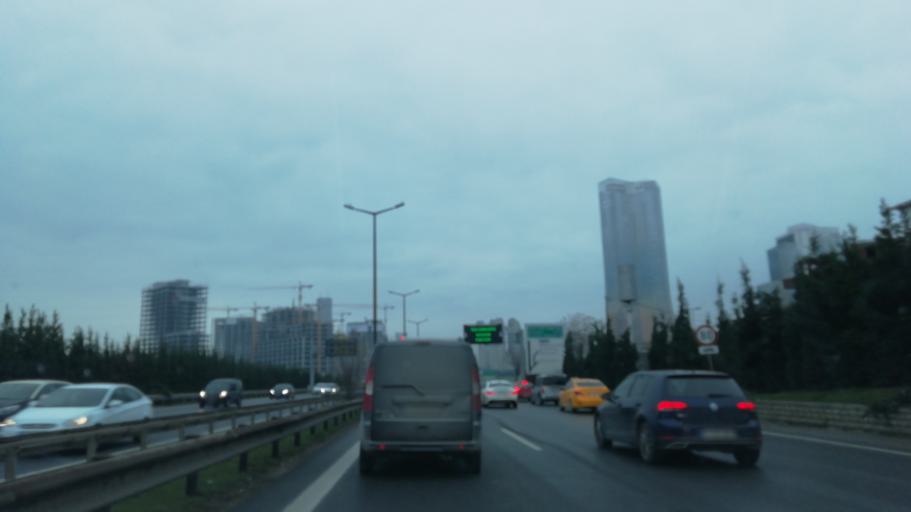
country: TR
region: Istanbul
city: Umraniye
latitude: 41.0060
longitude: 29.0992
